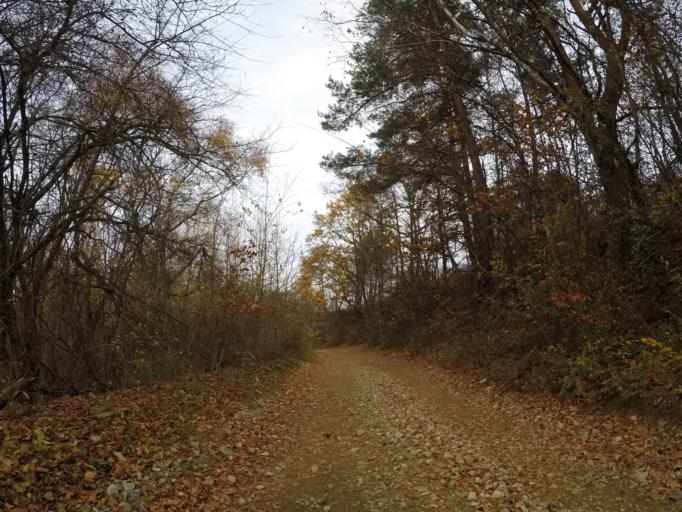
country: SK
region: Presovsky
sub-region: Okres Presov
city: Presov
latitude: 48.9228
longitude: 21.1440
